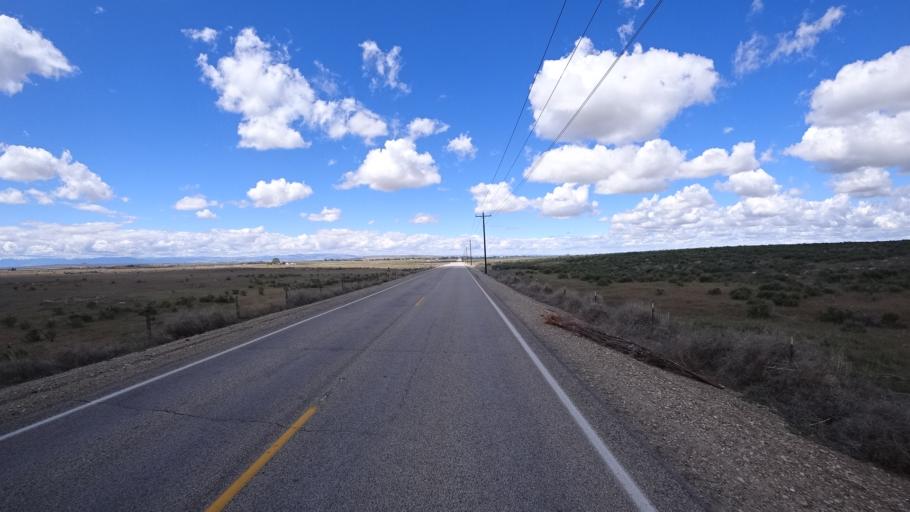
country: US
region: Idaho
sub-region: Ada County
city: Kuna
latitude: 43.4592
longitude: -116.3018
